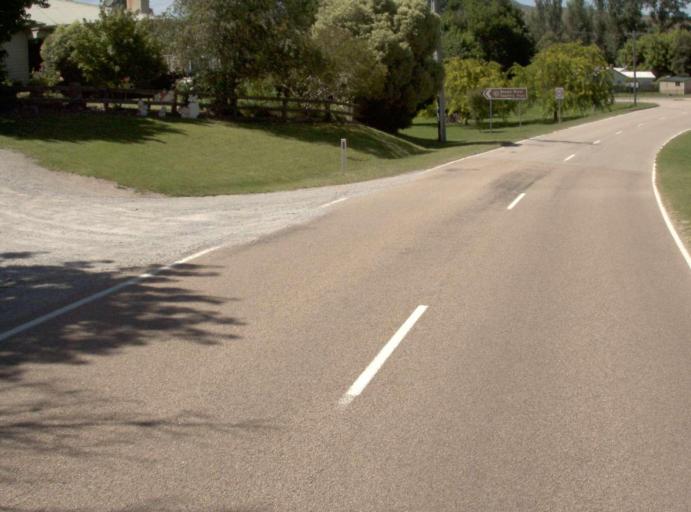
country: AU
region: Victoria
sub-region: East Gippsland
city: Lakes Entrance
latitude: -37.4940
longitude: 148.1739
